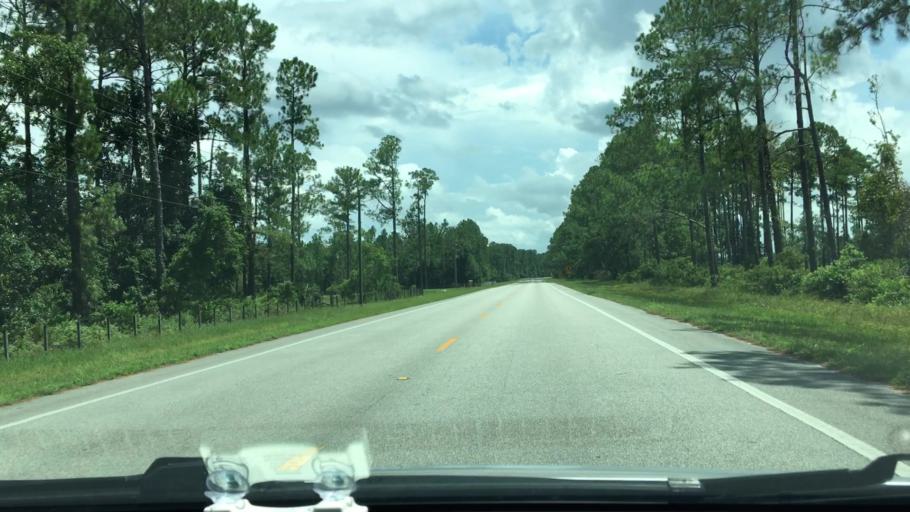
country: US
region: Florida
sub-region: Volusia County
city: Samsula-Spruce Creek
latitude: 29.0337
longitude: -81.0668
